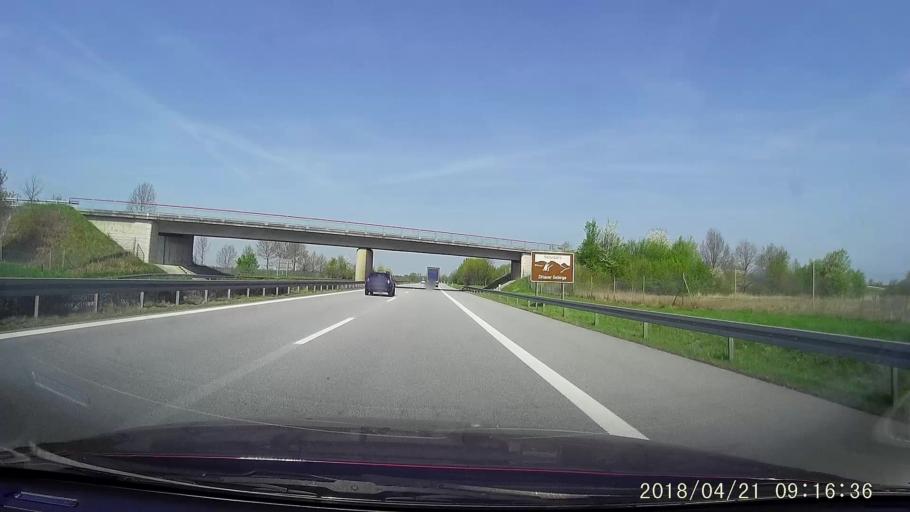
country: DE
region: Saxony
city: Weissenberg
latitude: 51.2098
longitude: 14.7307
